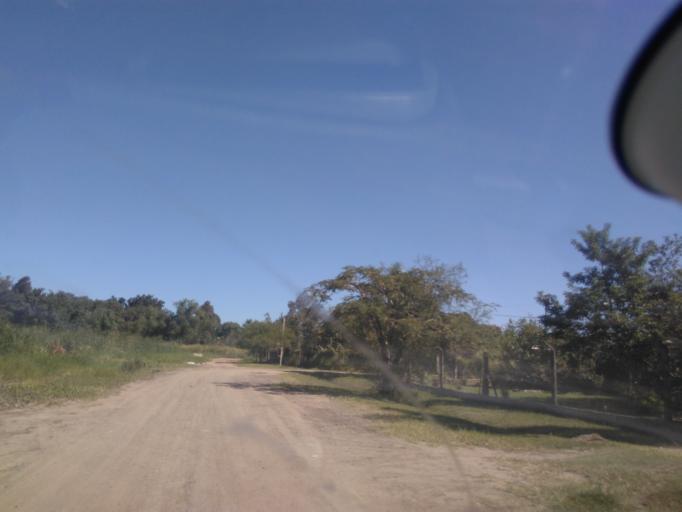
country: AR
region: Chaco
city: Fontana
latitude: -27.4294
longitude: -58.9974
